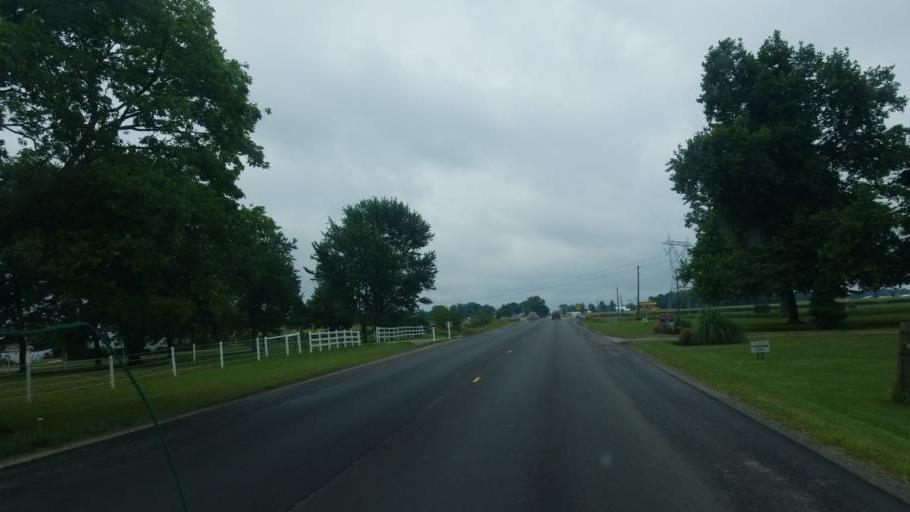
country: US
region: Indiana
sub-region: Adams County
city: Berne
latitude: 40.7052
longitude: -84.9559
